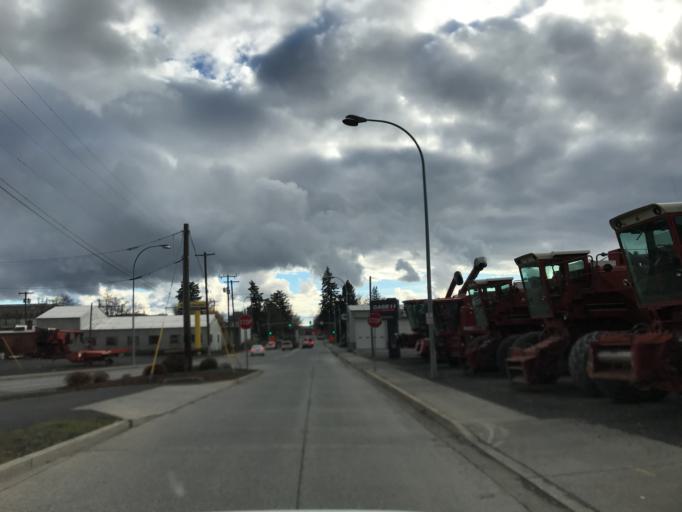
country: US
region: Idaho
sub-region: Latah County
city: Moscow
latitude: 46.7359
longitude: -117.0028
